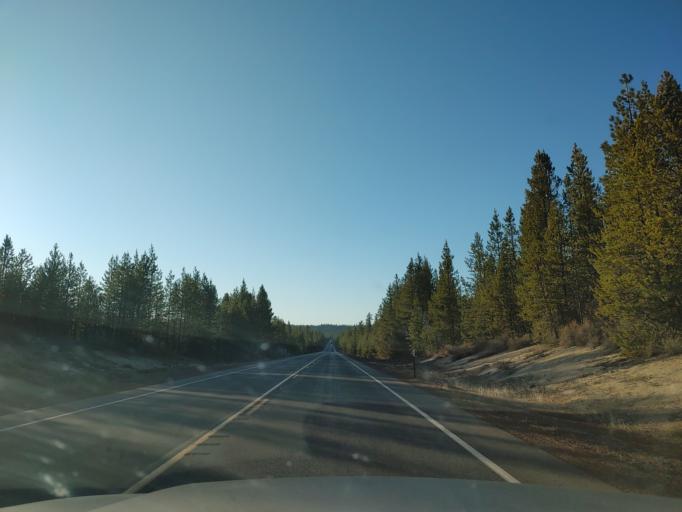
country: US
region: Oregon
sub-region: Deschutes County
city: La Pine
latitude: 43.4260
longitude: -121.8476
